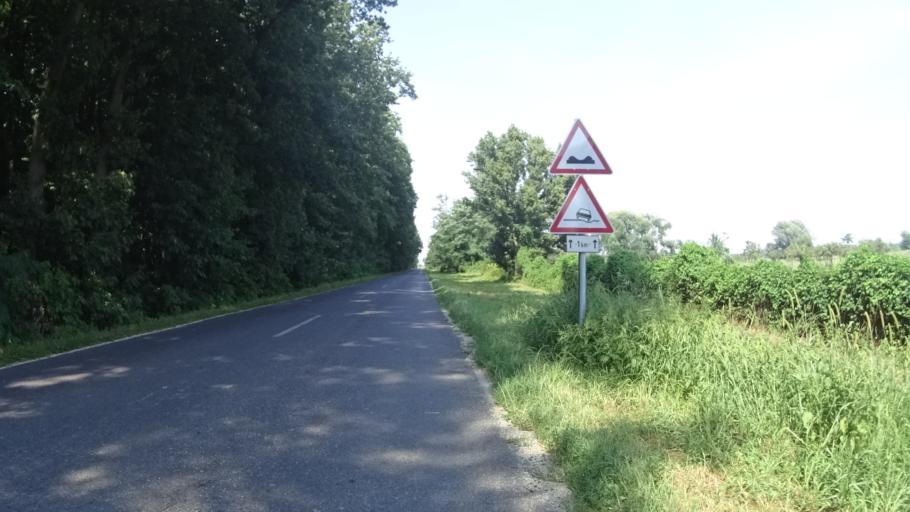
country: HU
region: Zala
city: Nagykanizsa
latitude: 46.4120
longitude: 16.9488
